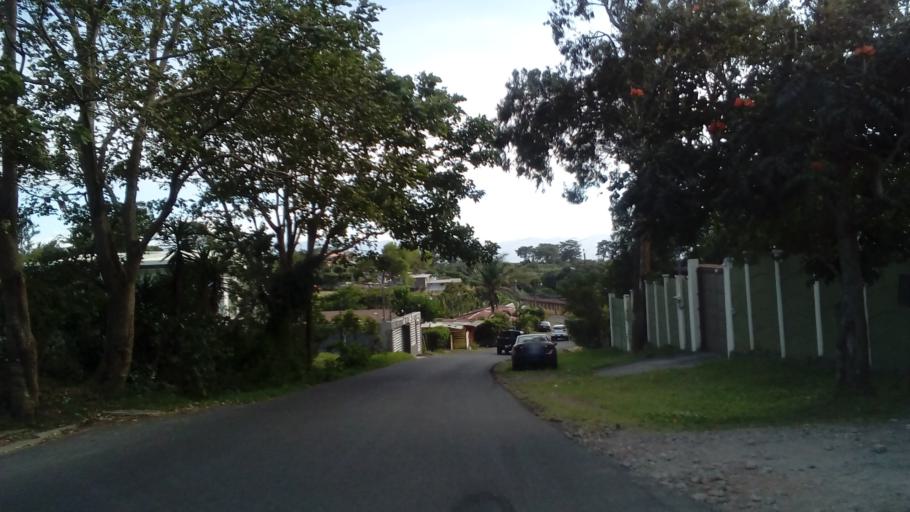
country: CR
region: Heredia
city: Angeles
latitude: 10.0000
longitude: -84.0522
